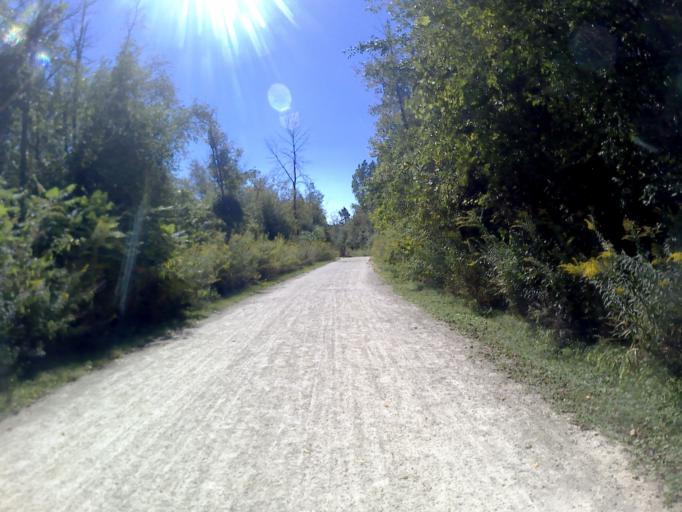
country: US
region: Illinois
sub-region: DuPage County
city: Warrenville
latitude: 41.7885
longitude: -88.1791
